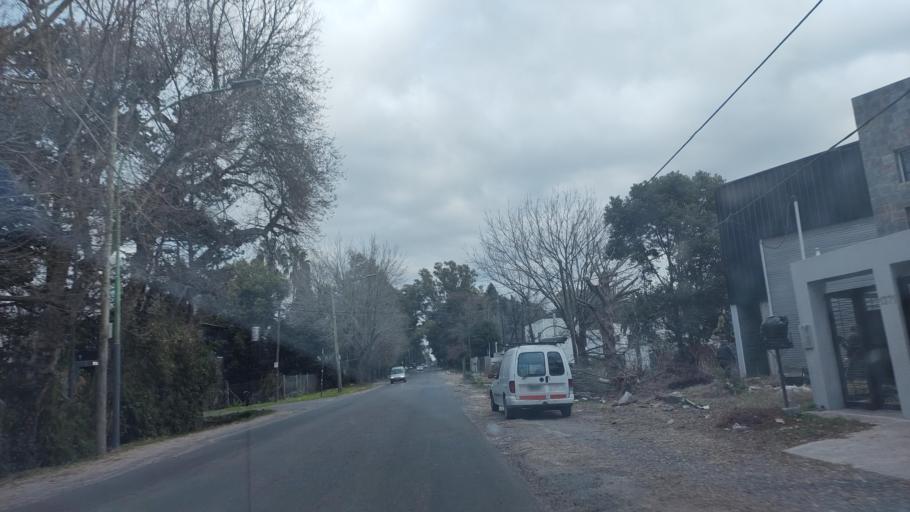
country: AR
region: Buenos Aires
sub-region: Partido de La Plata
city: La Plata
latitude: -34.8591
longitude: -58.0857
